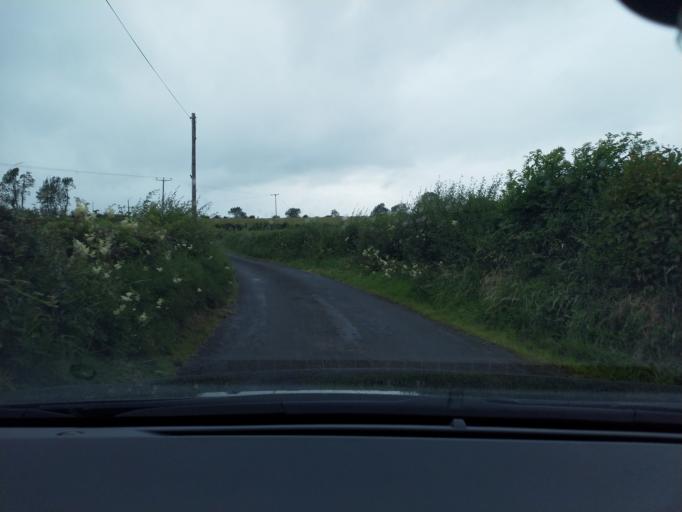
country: GB
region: Northern Ireland
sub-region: Dungannon District
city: Dungannon
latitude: 54.4030
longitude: -6.7761
